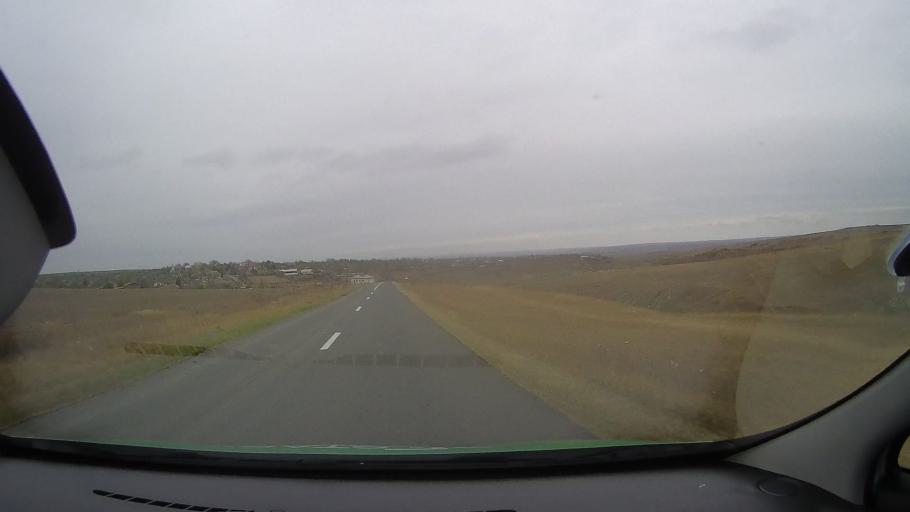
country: RO
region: Constanta
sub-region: Comuna Pantelimon
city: Pantelimon
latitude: 44.5380
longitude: 28.3282
